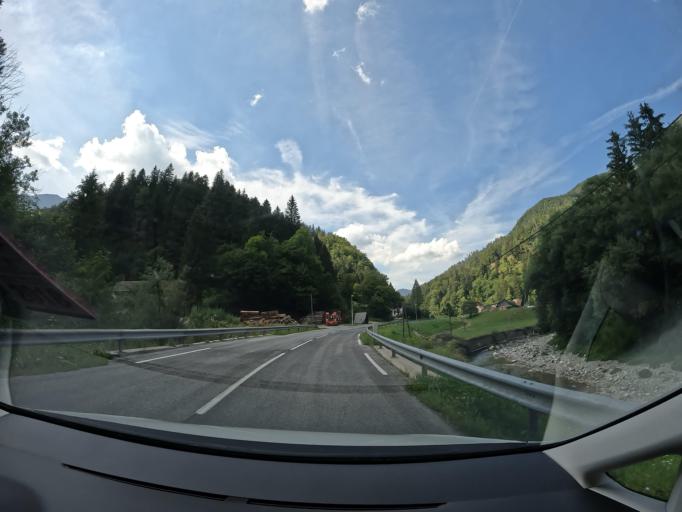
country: SI
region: Jezersko
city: Zgornje Jezersko
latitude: 46.3382
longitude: 14.4869
